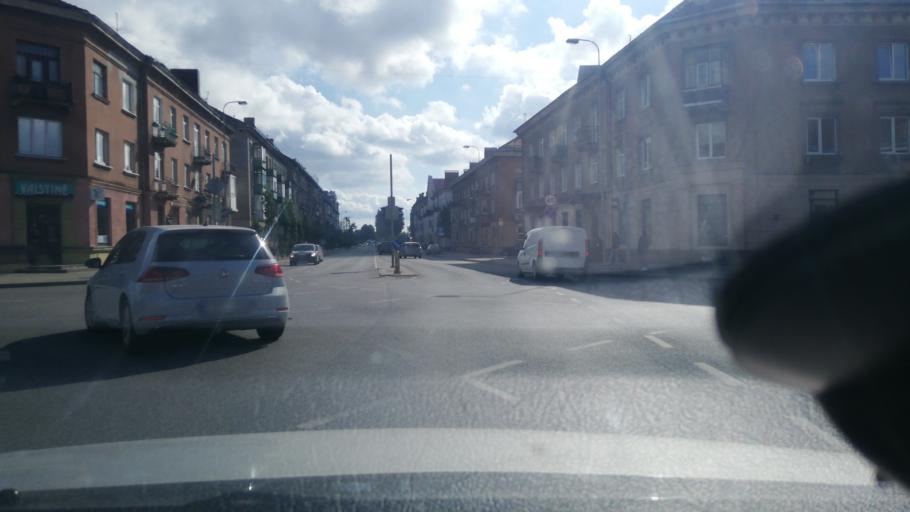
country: LT
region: Klaipedos apskritis
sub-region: Klaipeda
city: Klaipeda
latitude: 55.6782
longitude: 21.1523
